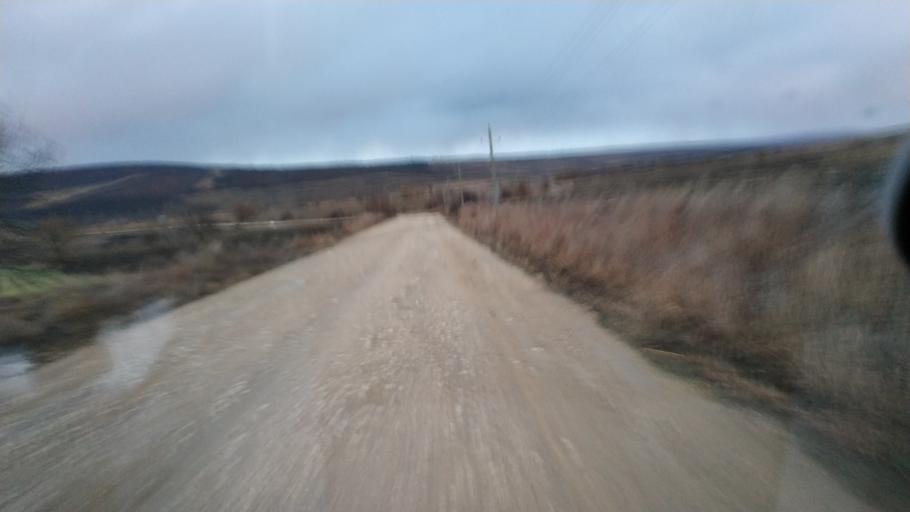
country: MD
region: Taraclia
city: Telenesti
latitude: 47.3881
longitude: 28.3295
